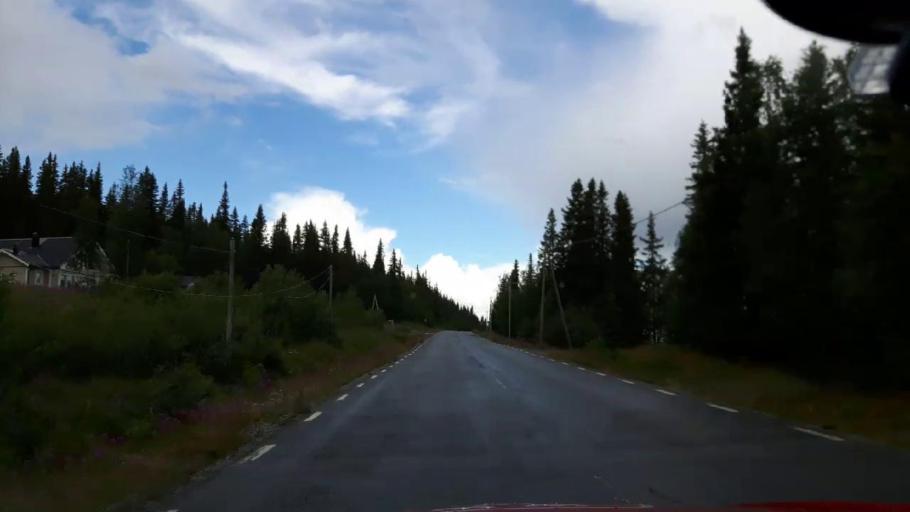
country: SE
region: Vaesterbotten
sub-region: Vilhelmina Kommun
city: Sjoberg
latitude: 64.9749
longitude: 15.3258
